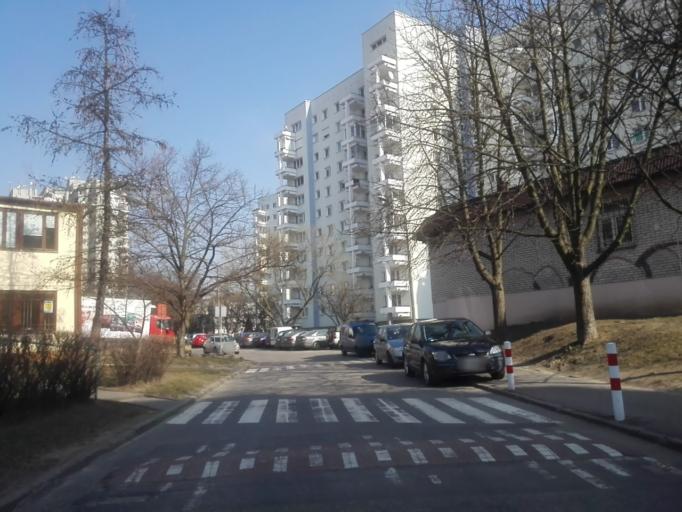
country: PL
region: Masovian Voivodeship
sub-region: Warszawa
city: Mokotow
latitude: 52.1719
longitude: 21.0205
